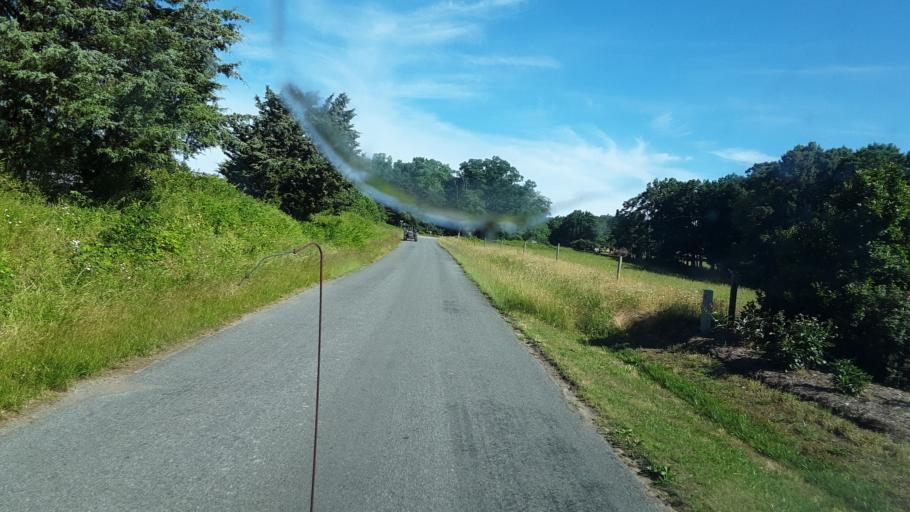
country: US
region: Virginia
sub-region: Pittsylvania County
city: Chatham
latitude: 36.8410
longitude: -79.4152
